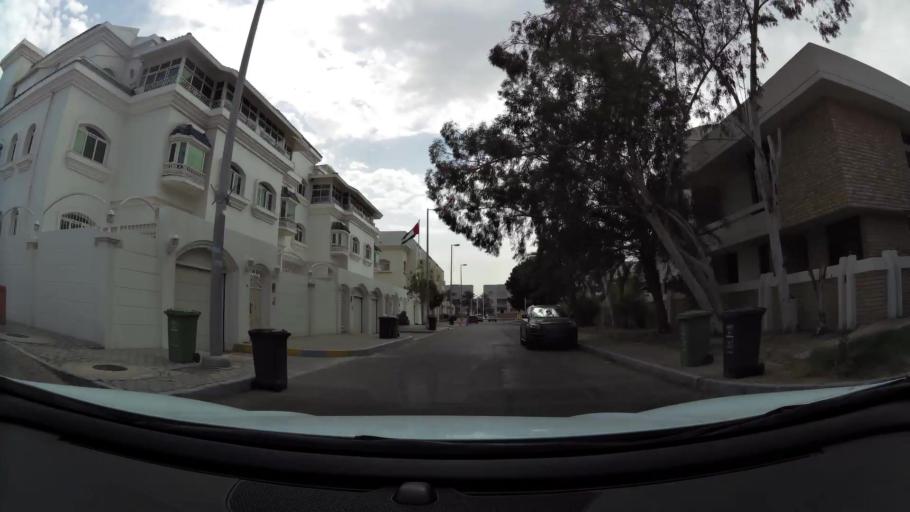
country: AE
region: Abu Dhabi
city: Abu Dhabi
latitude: 24.4496
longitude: 54.3581
